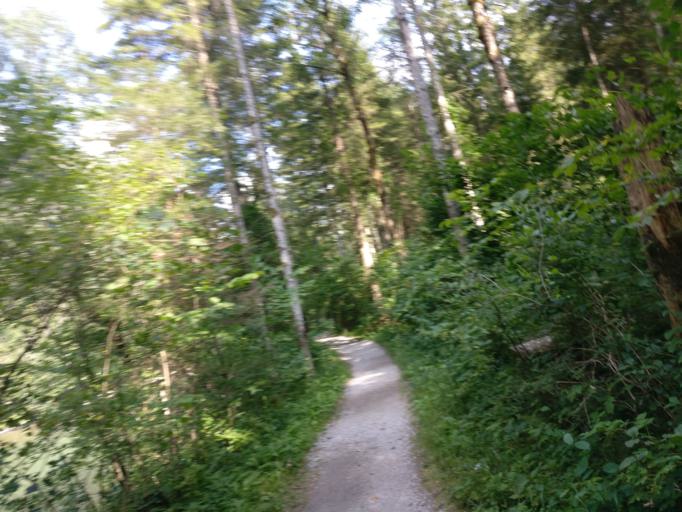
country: AT
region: Styria
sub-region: Politischer Bezirk Liezen
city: Johnsbach
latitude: 47.5830
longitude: 14.5864
